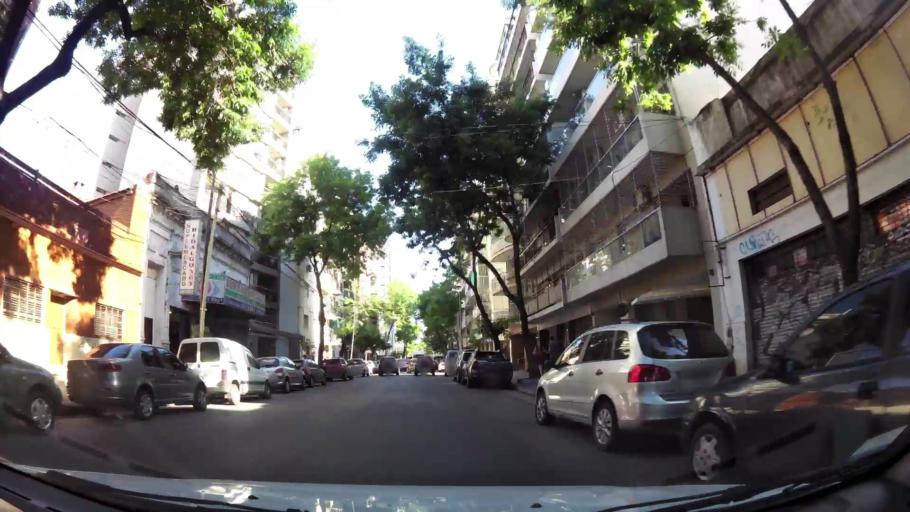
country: AR
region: Buenos Aires F.D.
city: Villa Santa Rita
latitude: -34.6150
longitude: -58.4395
